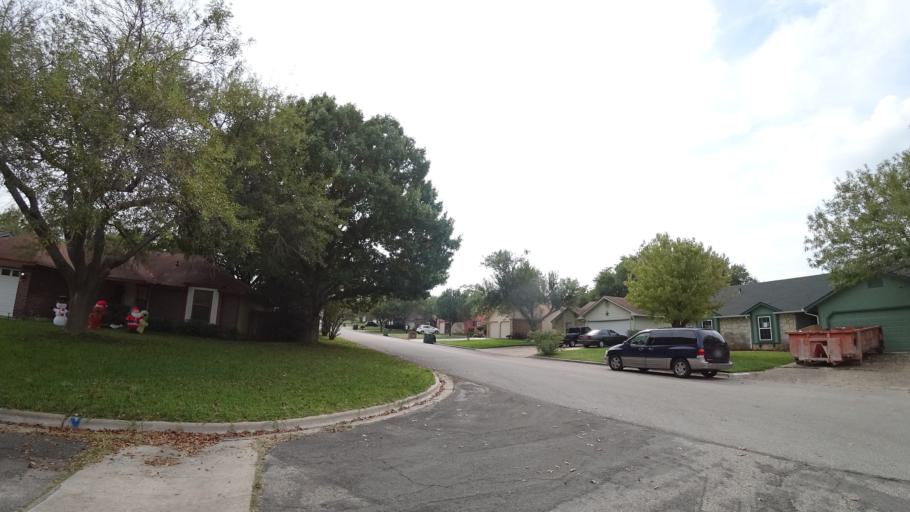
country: US
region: Texas
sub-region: Williamson County
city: Round Rock
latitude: 30.4912
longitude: -97.6841
